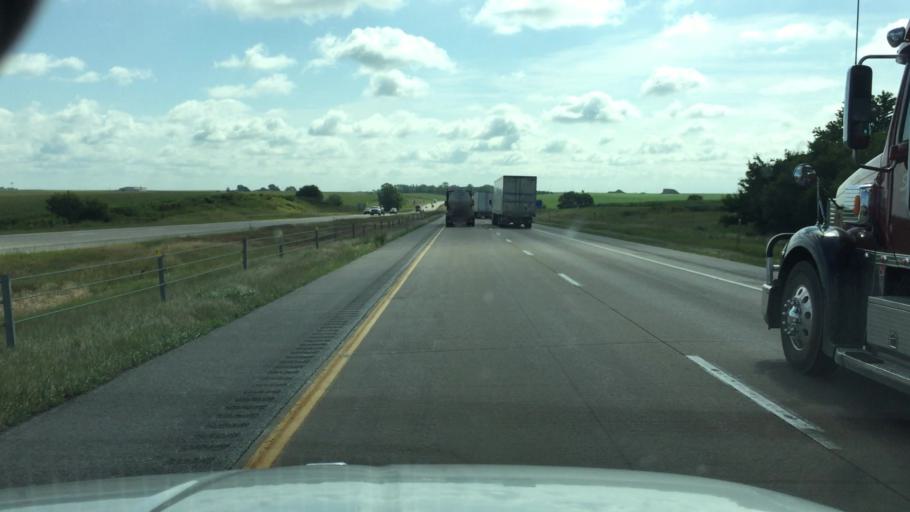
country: US
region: Iowa
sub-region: Cedar County
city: Durant
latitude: 41.6340
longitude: -90.9393
